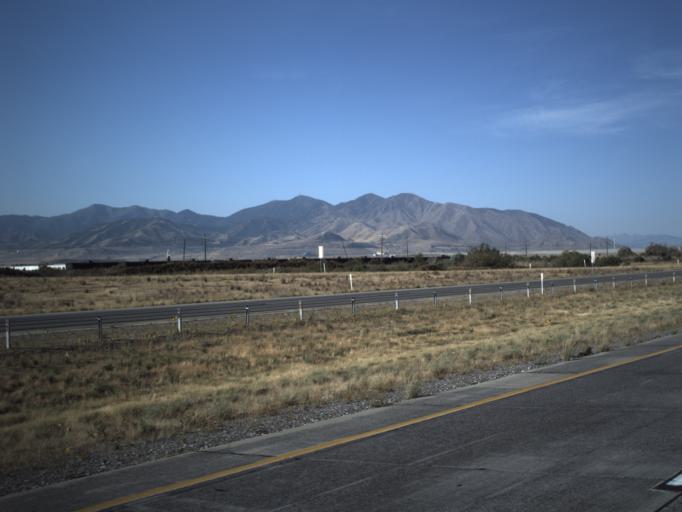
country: US
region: Utah
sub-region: Salt Lake County
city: West Valley City
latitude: 40.7712
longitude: -112.0292
